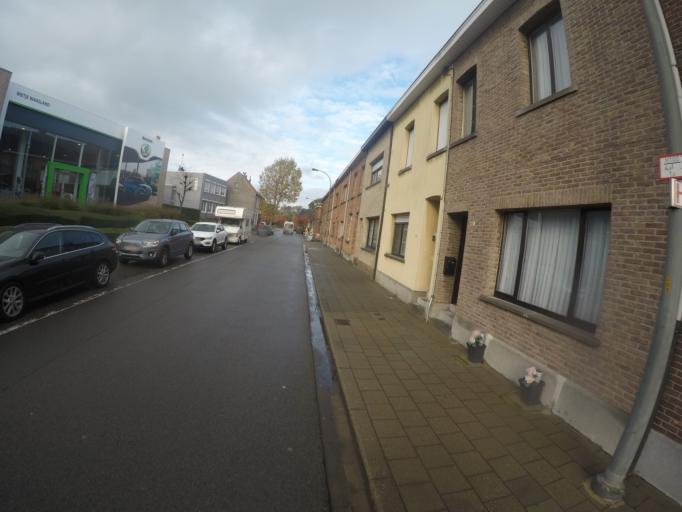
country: BE
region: Flanders
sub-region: Provincie Antwerpen
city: Zwijndrecht
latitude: 51.2099
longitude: 4.3336
